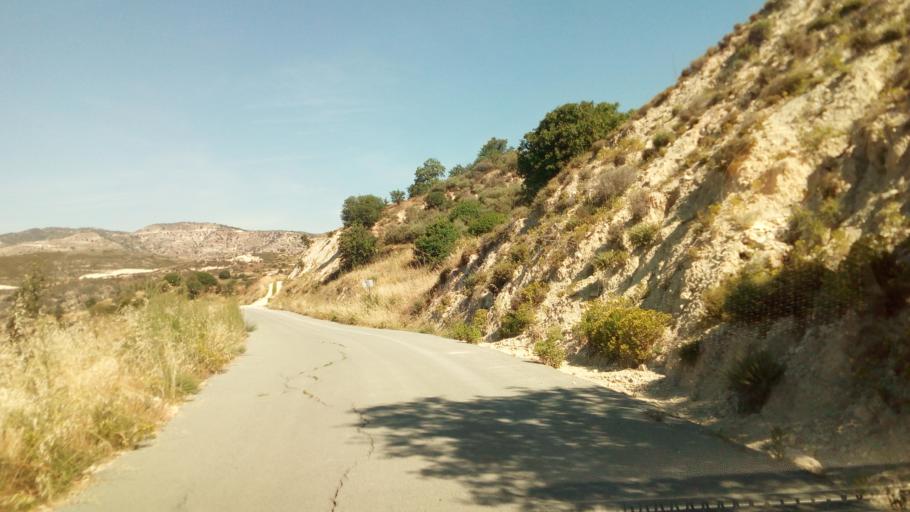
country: CY
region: Limassol
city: Pachna
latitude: 34.8142
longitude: 32.7365
